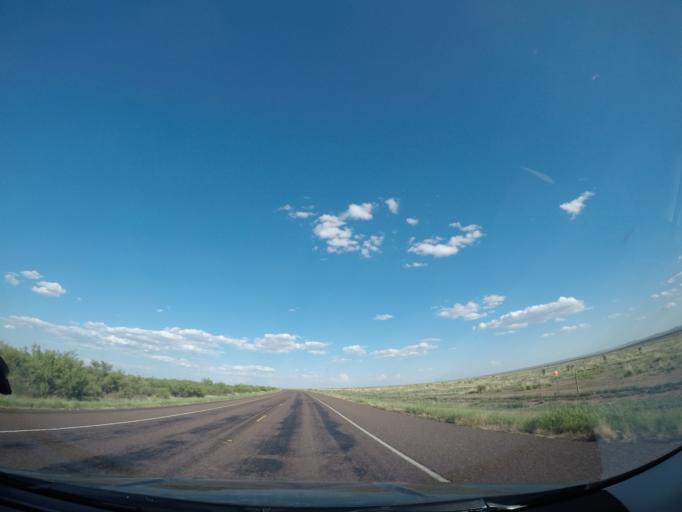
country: US
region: Texas
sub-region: Presidio County
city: Marfa
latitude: 30.3812
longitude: -104.2377
